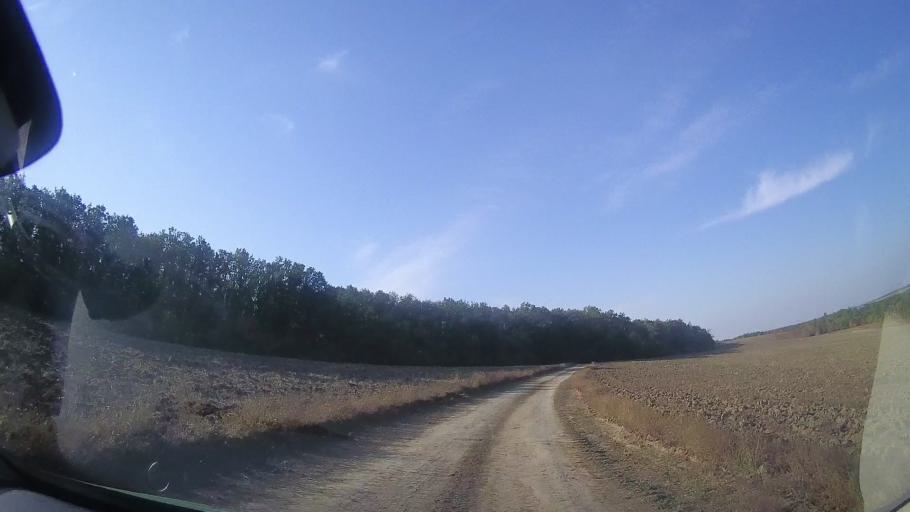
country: RO
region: Timis
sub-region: Comuna Bogda
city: Bogda
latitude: 45.9079
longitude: 21.5841
